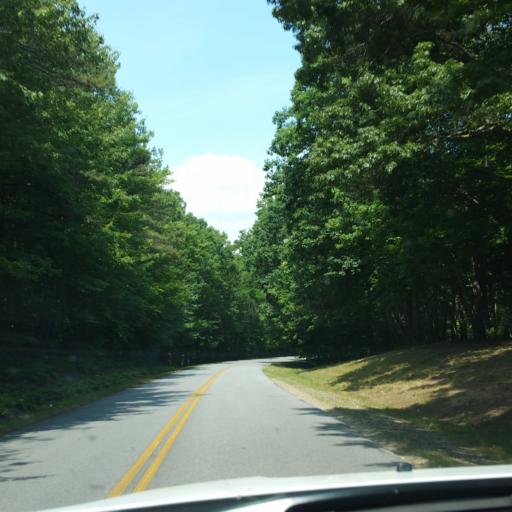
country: US
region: North Carolina
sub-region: Buncombe County
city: Avery Creek
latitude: 35.4981
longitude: -82.5703
